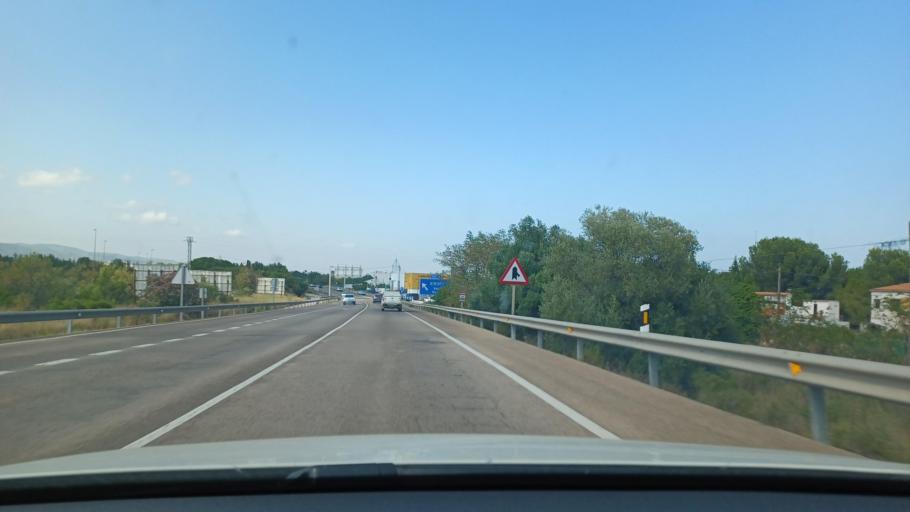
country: ES
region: Valencia
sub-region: Provincia de Castello
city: Orpesa/Oropesa del Mar
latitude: 40.0971
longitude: 0.1334
